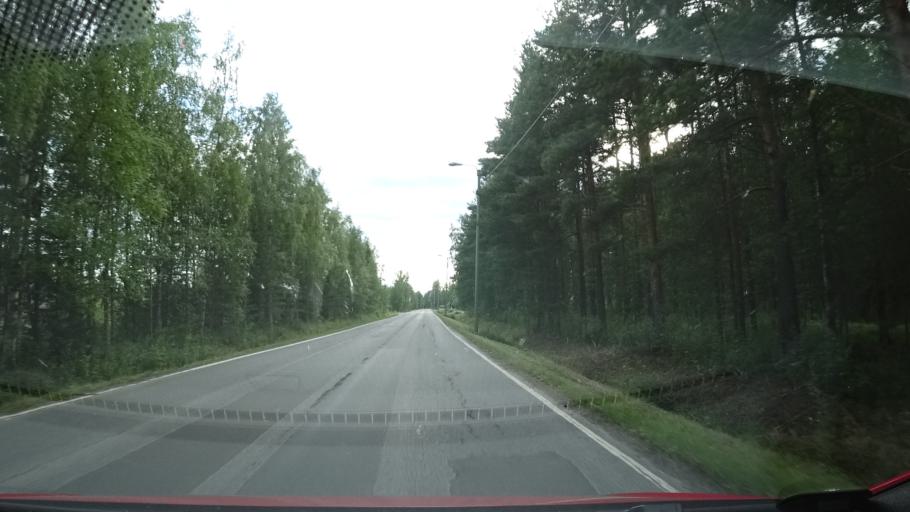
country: FI
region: Northern Ostrobothnia
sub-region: Oulu
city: Liminka
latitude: 64.8083
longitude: 25.4496
